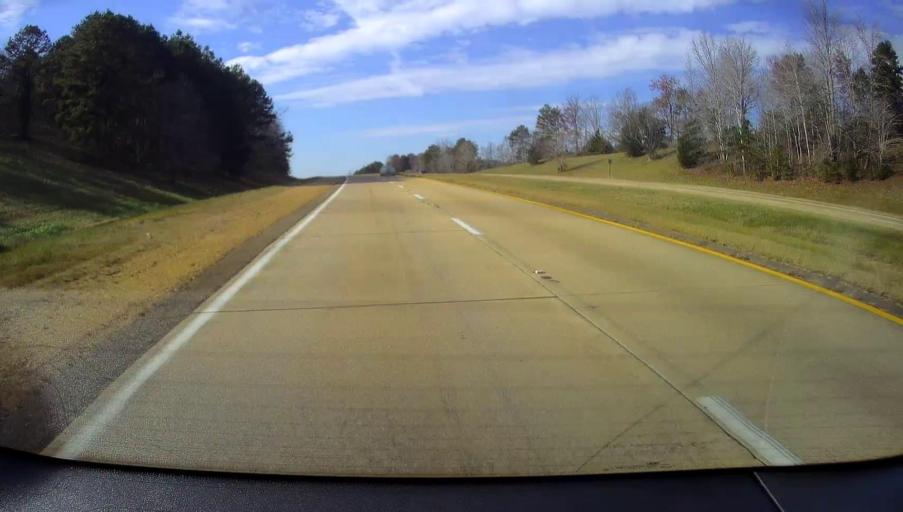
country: US
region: Mississippi
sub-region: Tishomingo County
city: Iuka
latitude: 34.7678
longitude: -88.1211
